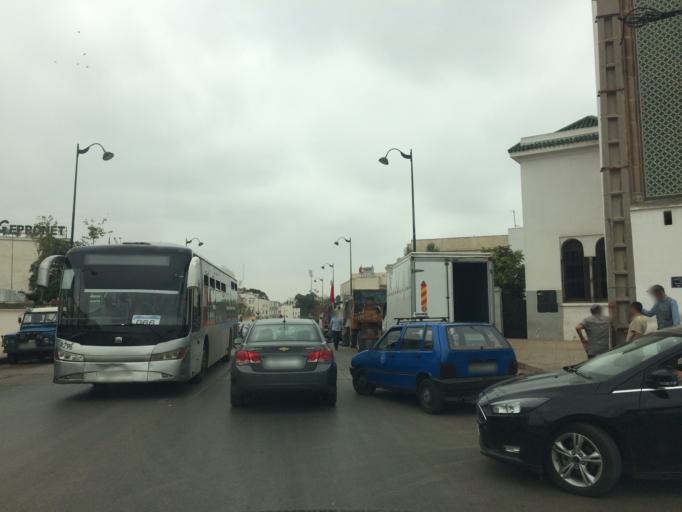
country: MA
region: Rabat-Sale-Zemmour-Zaer
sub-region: Rabat
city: Rabat
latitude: 33.9810
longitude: -6.8262
